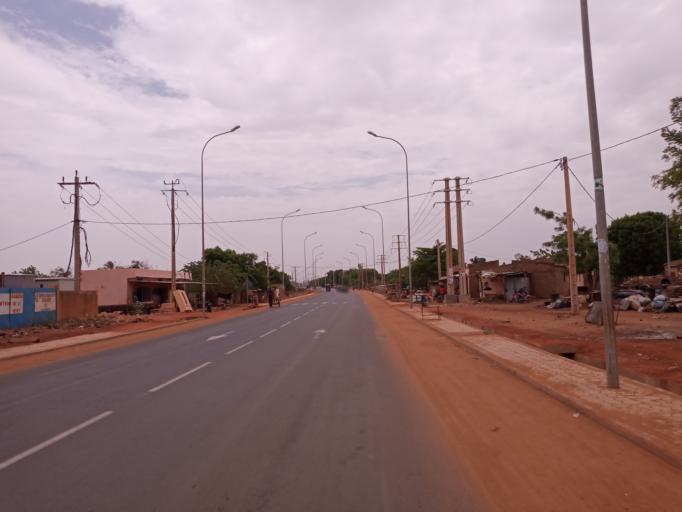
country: ML
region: Koulikoro
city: Koulikoro
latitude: 12.8527
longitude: -7.5687
